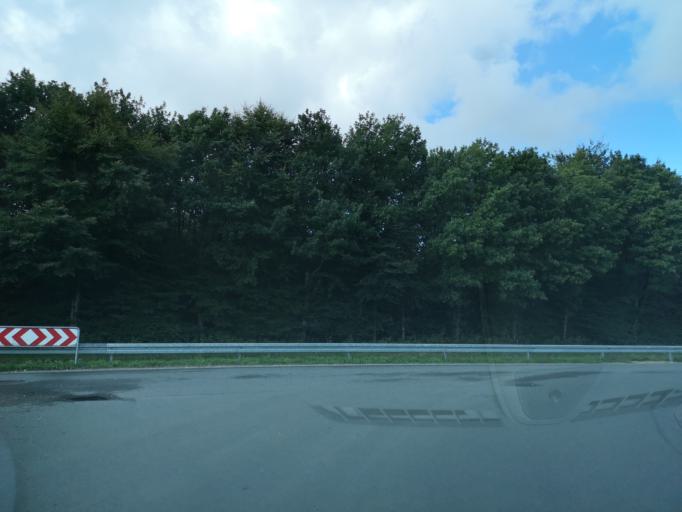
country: DK
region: Central Jutland
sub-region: Holstebro Kommune
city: Holstebro
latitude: 56.3337
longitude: 8.6474
